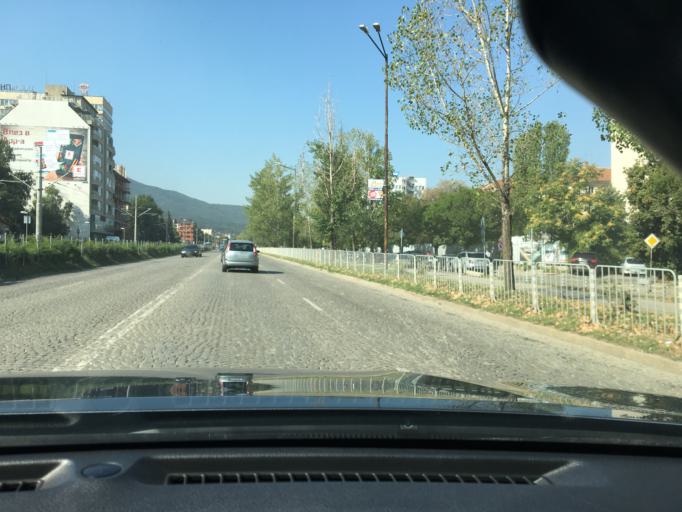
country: BG
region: Sofia-Capital
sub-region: Stolichna Obshtina
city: Sofia
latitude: 42.6699
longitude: 23.2693
